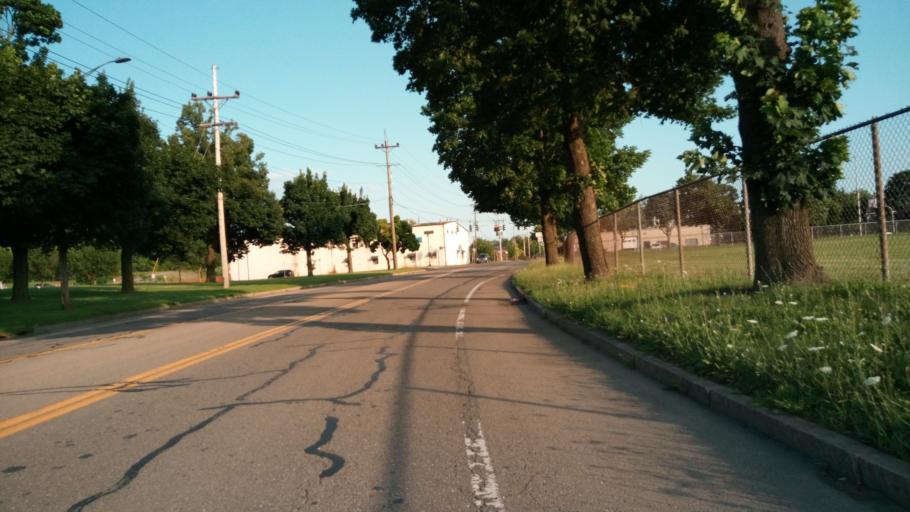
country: US
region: New York
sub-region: Chemung County
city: Elmira
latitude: 42.0957
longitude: -76.7923
